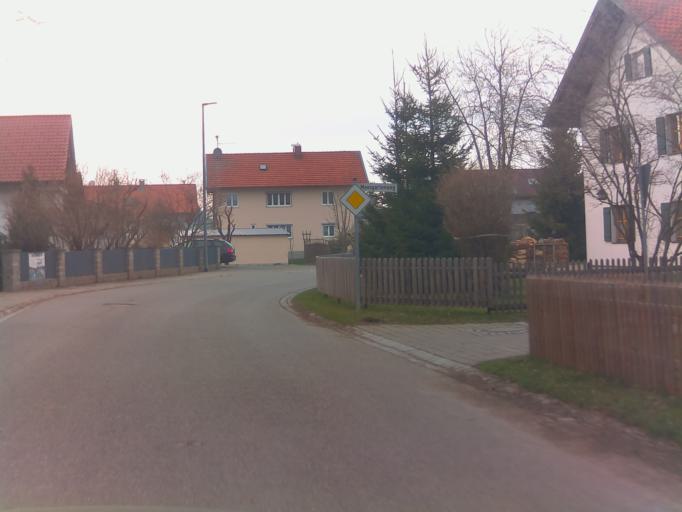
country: DE
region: Bavaria
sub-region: Upper Bavaria
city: Ingenried
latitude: 47.8167
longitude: 10.7817
